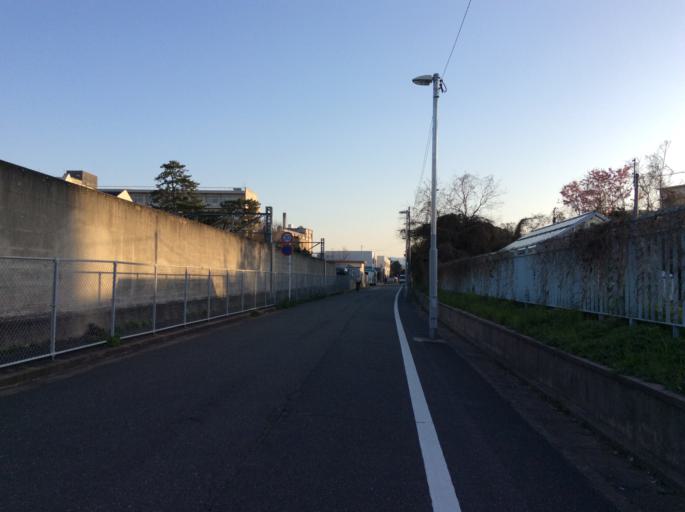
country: JP
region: Fukuoka
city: Fukuoka-shi
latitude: 33.6284
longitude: 130.4244
